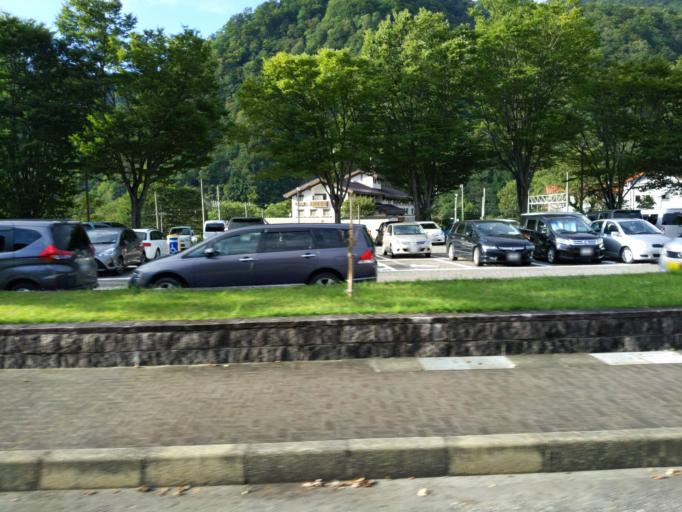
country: JP
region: Toyama
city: Kamiichi
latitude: 36.5822
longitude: 137.4438
